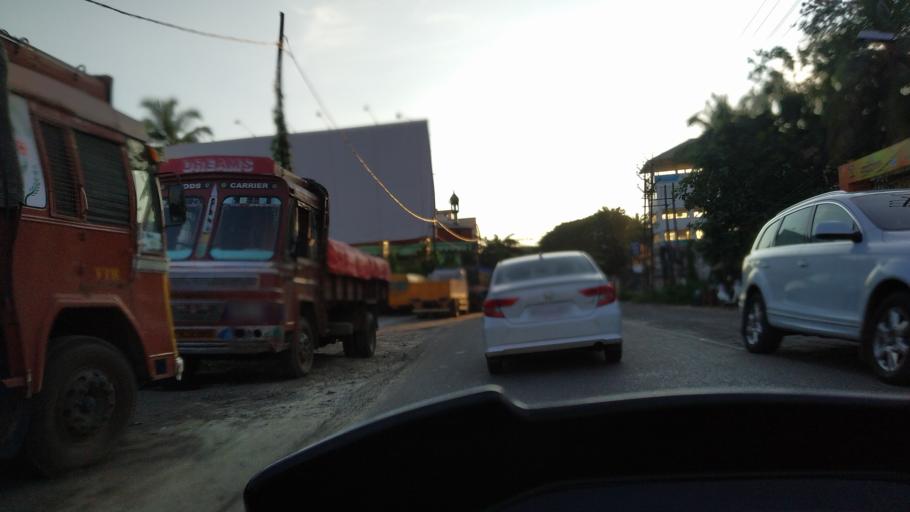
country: IN
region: Kerala
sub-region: Ernakulam
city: Cochin
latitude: 9.9513
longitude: 76.3351
